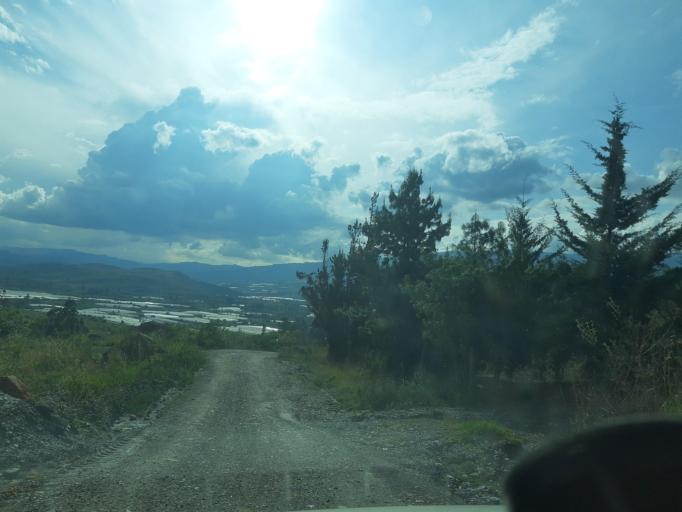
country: CO
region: Boyaca
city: Villa de Leiva
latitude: 5.6658
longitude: -73.5627
